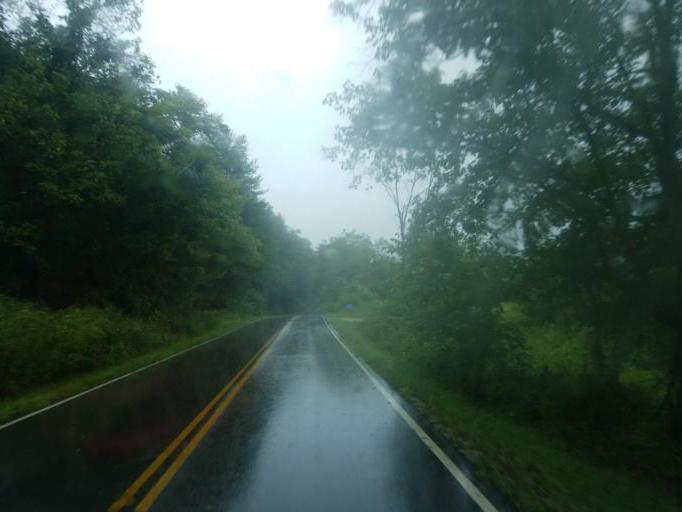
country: US
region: Kentucky
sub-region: Greenup County
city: Greenup
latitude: 38.4970
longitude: -82.9716
